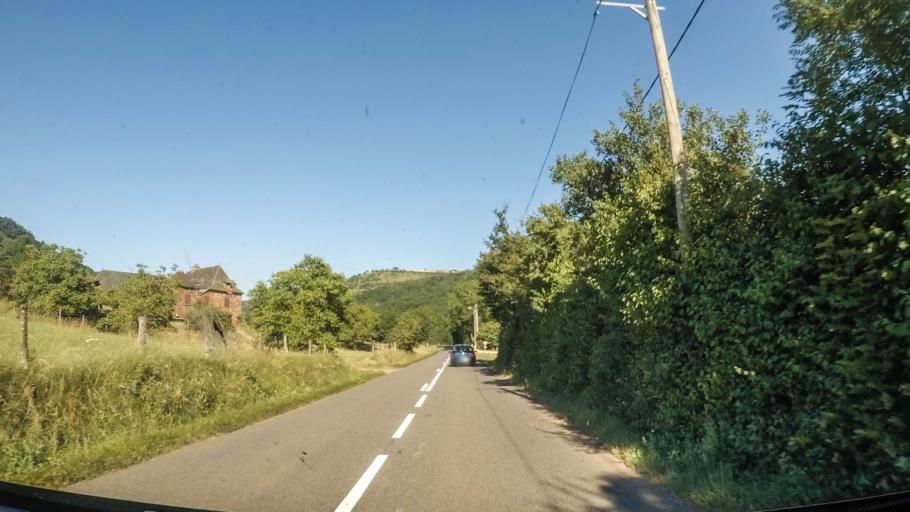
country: FR
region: Midi-Pyrenees
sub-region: Departement de l'Aveyron
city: Valady
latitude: 44.4642
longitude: 2.4258
